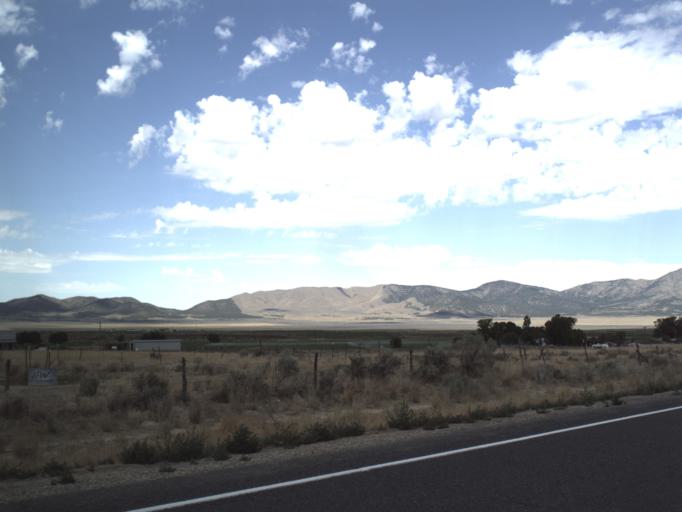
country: US
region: Utah
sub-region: Tooele County
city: Tooele
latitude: 40.0870
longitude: -112.4282
